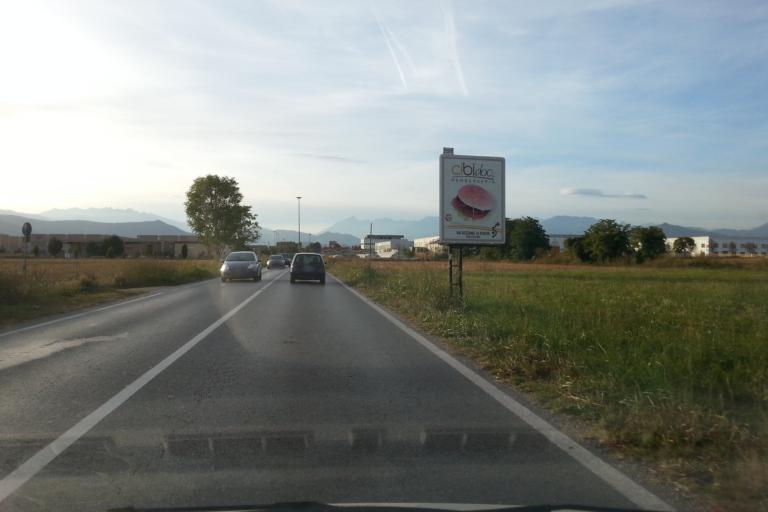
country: IT
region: Piedmont
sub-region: Provincia di Torino
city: Pasta
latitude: 44.9968
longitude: 7.5574
